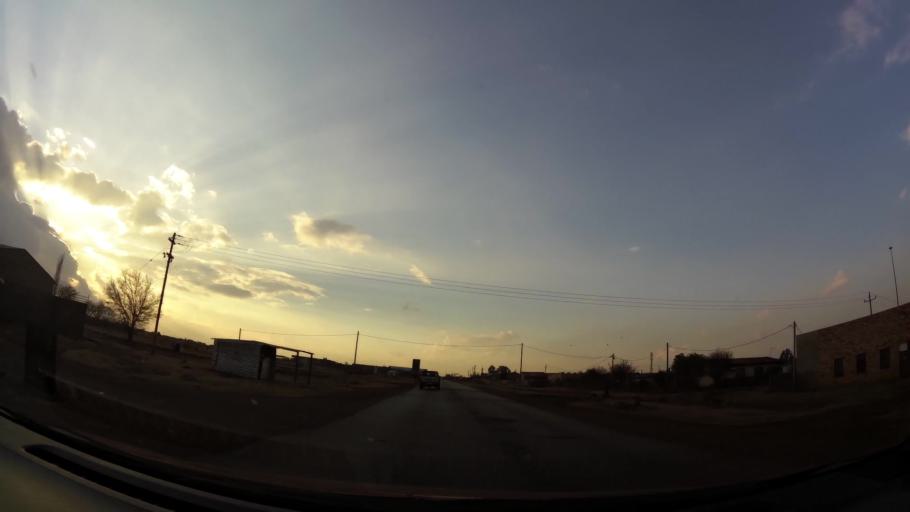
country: ZA
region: Gauteng
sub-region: City of Johannesburg Metropolitan Municipality
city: Orange Farm
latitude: -26.5414
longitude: 27.8328
